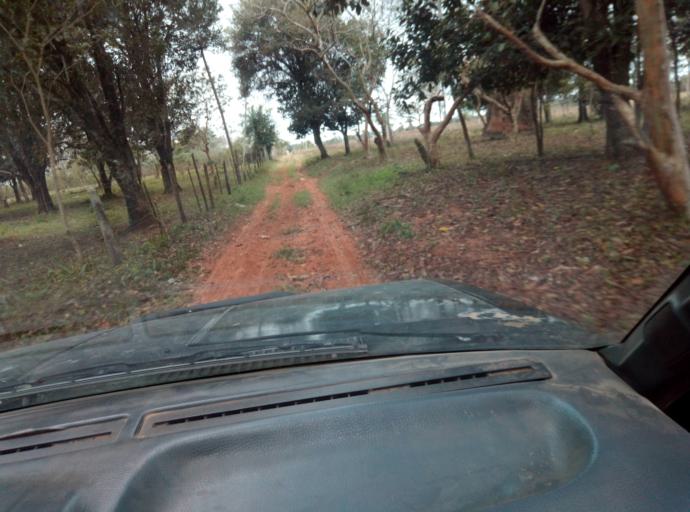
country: PY
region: Caaguazu
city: Doctor Cecilio Baez
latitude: -25.1444
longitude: -56.2979
